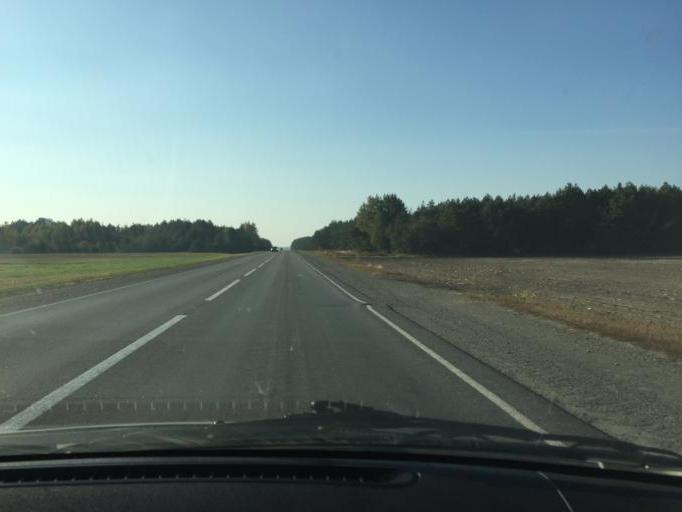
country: BY
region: Brest
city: Davyd-Haradok
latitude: 52.2377
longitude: 27.2238
